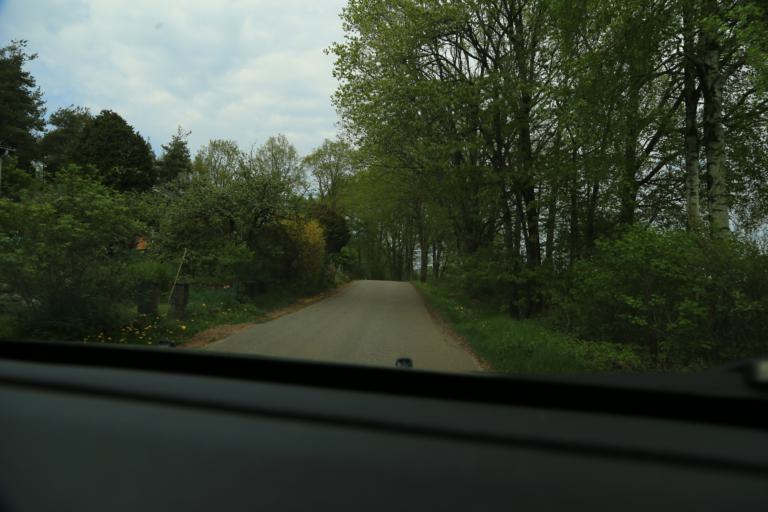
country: SE
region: Halland
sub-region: Varbergs Kommun
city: Varberg
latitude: 57.1451
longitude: 12.2277
